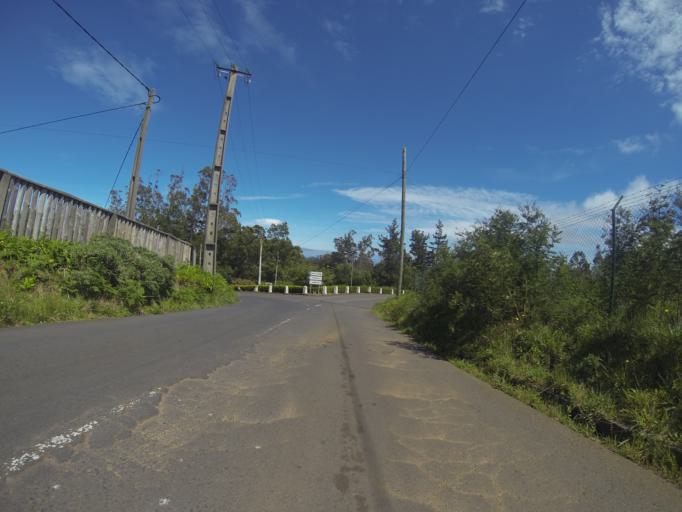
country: PT
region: Madeira
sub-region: Santa Cruz
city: Camacha
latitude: 32.7176
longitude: -16.8327
